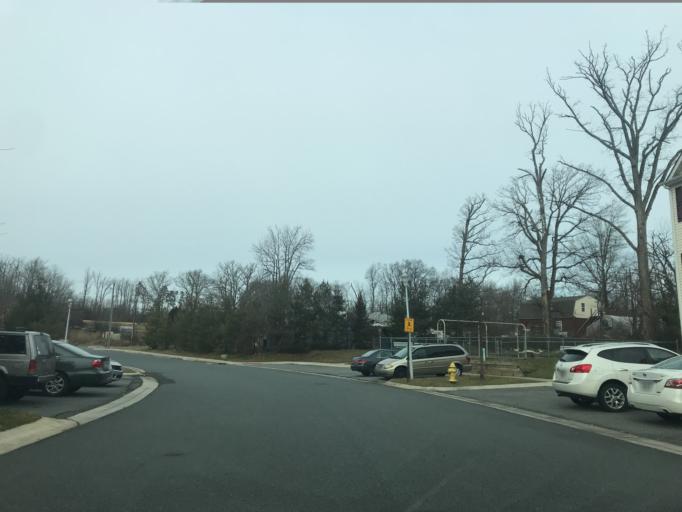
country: US
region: Maryland
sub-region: Cecil County
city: Elkton
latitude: 39.6144
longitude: -75.8052
